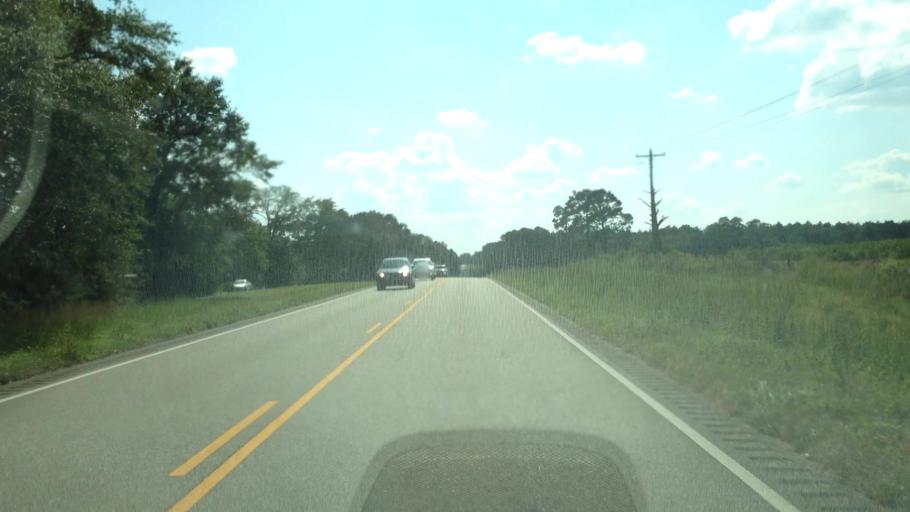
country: US
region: Alabama
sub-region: Covington County
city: Florala
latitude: 31.0400
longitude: -86.5980
